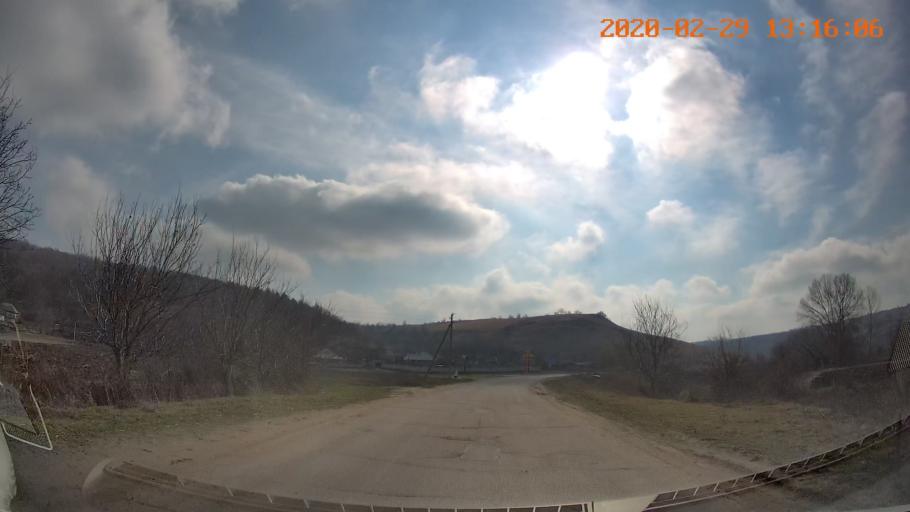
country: MD
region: Telenesti
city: Camenca
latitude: 48.0052
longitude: 28.6666
